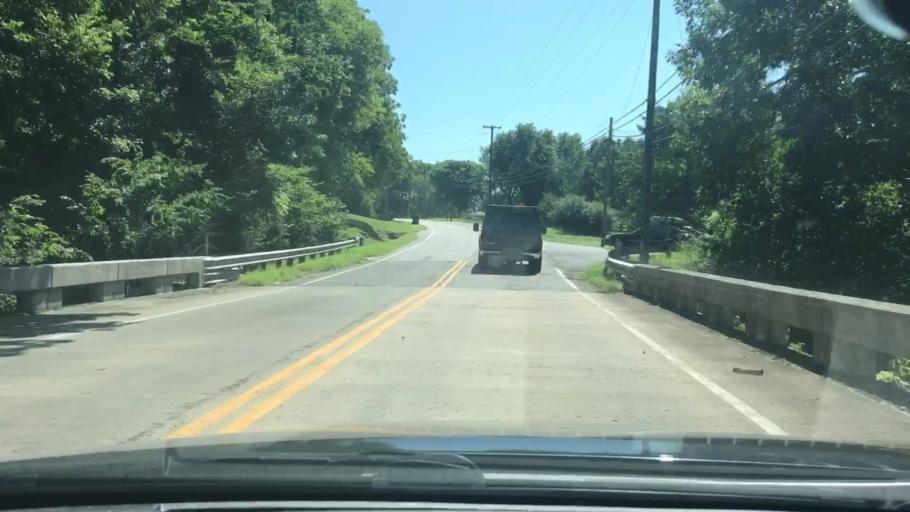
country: US
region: Tennessee
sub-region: Sumner County
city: Gallatin
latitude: 36.3946
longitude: -86.4688
